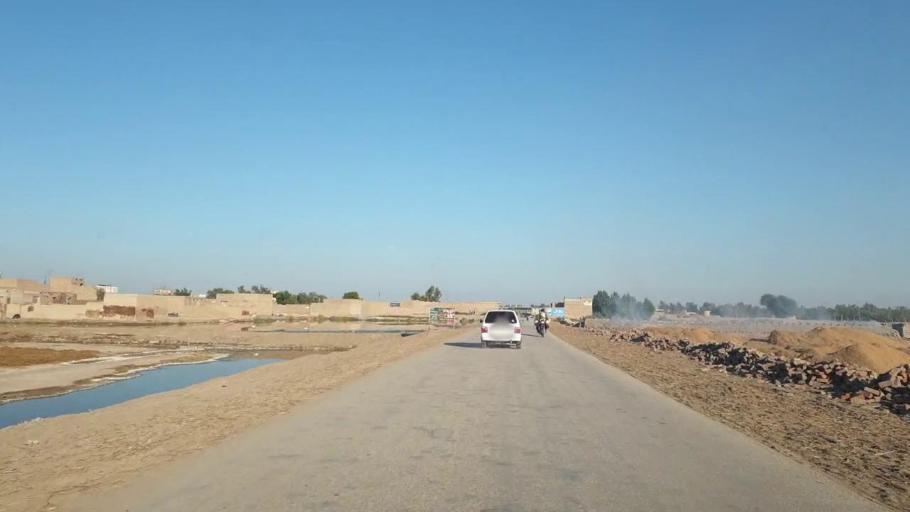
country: PK
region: Sindh
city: Dokri
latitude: 27.3678
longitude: 68.1028
